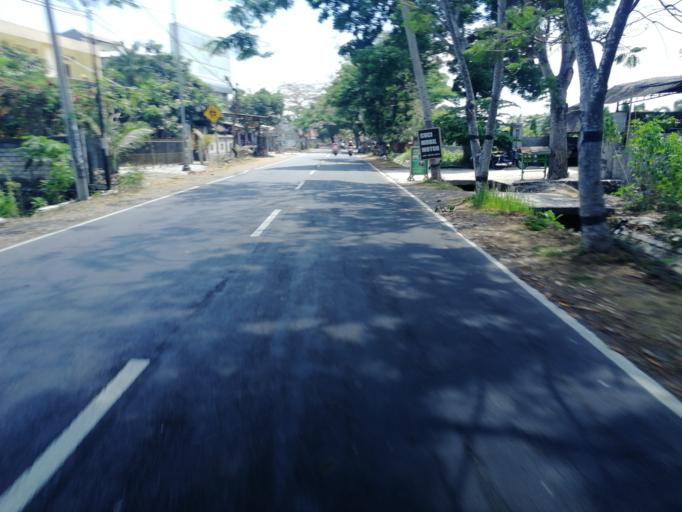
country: ID
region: West Nusa Tenggara
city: Jelateng Timur
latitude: -8.7058
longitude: 116.0864
